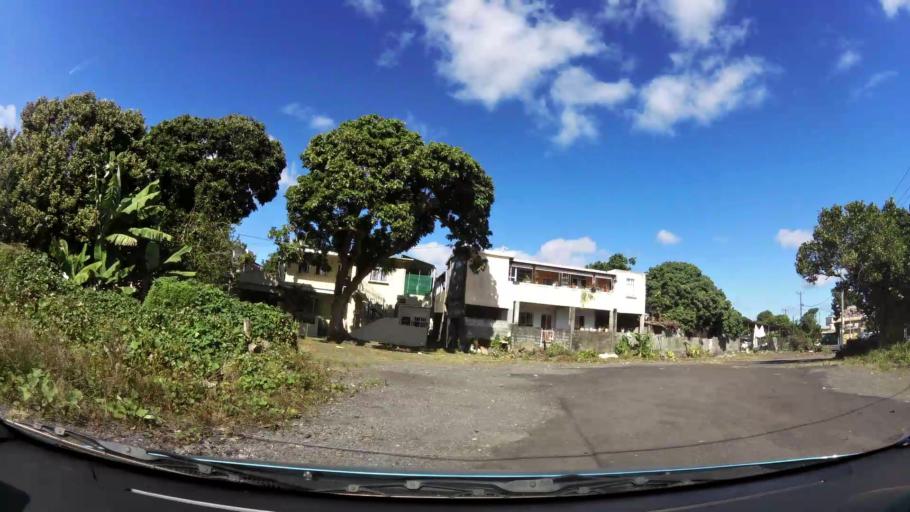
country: MU
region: Plaines Wilhems
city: Vacoas
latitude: -20.3133
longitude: 57.4877
